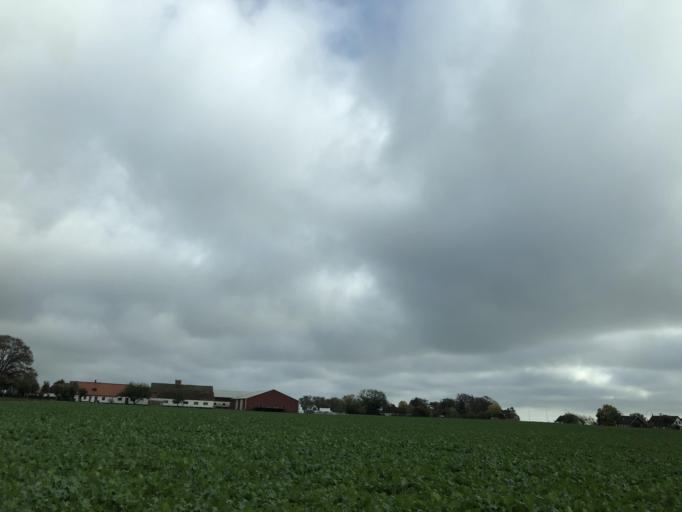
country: SE
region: Skane
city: Smygehamn
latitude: 55.3459
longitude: 13.3154
